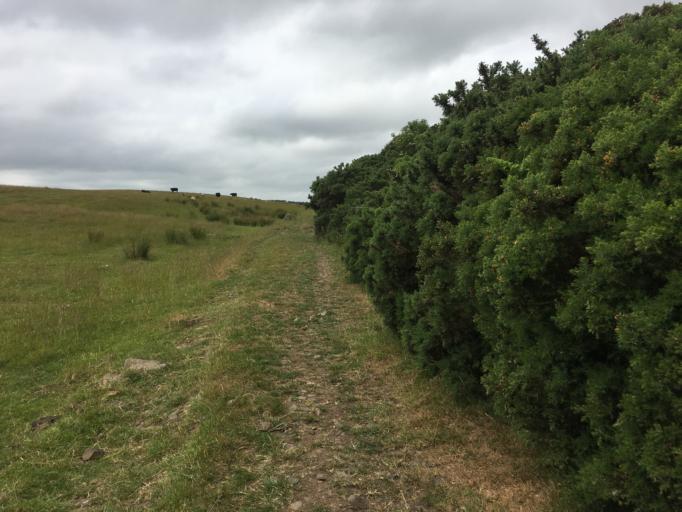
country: GB
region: England
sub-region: Northumberland
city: Belford
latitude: 55.6136
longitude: -1.8929
